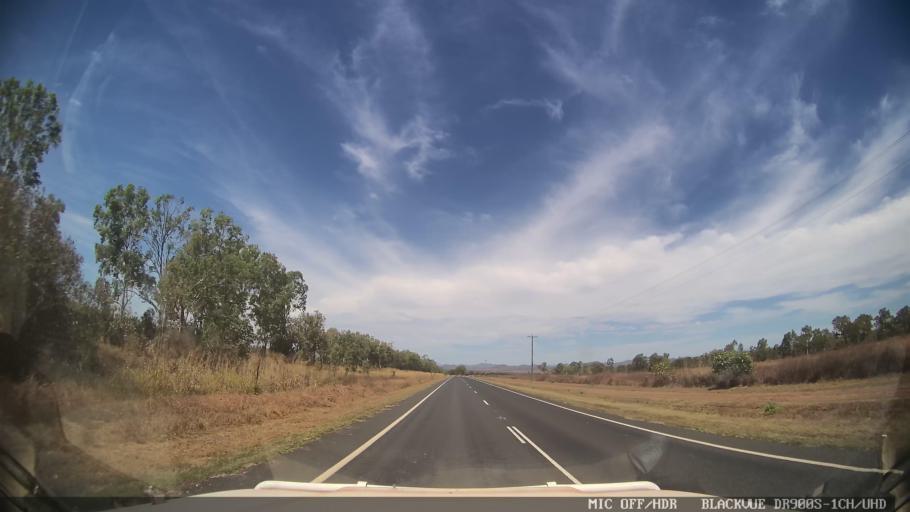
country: AU
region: Queensland
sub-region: Cook
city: Cooktown
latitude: -15.8394
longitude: 144.8532
